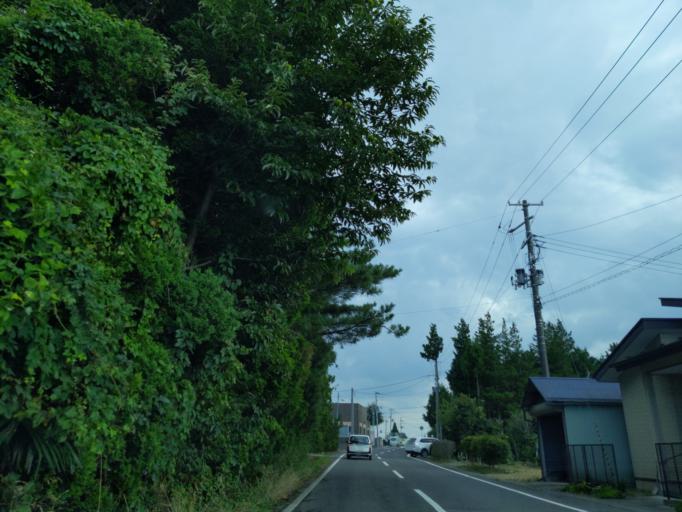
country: JP
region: Fukushima
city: Sukagawa
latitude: 37.3093
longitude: 140.3380
